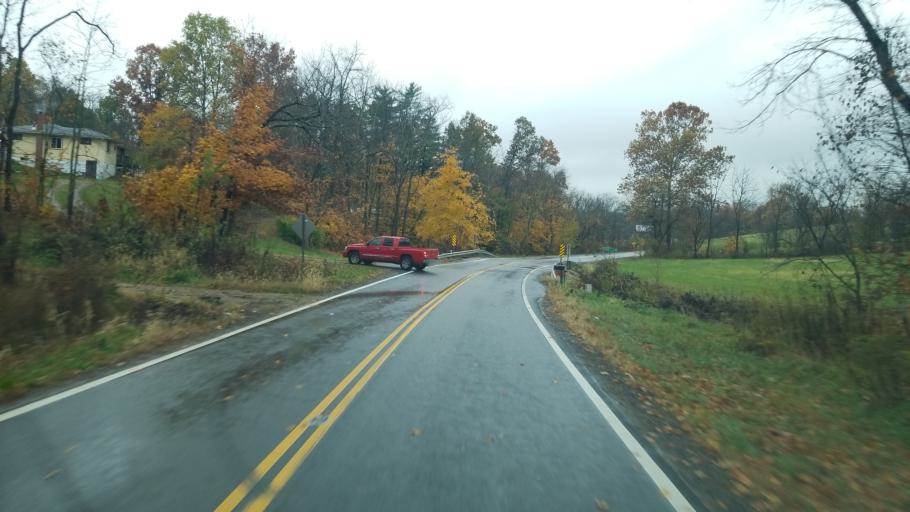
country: US
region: Ohio
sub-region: Coshocton County
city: Coshocton
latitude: 40.3404
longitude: -81.8607
